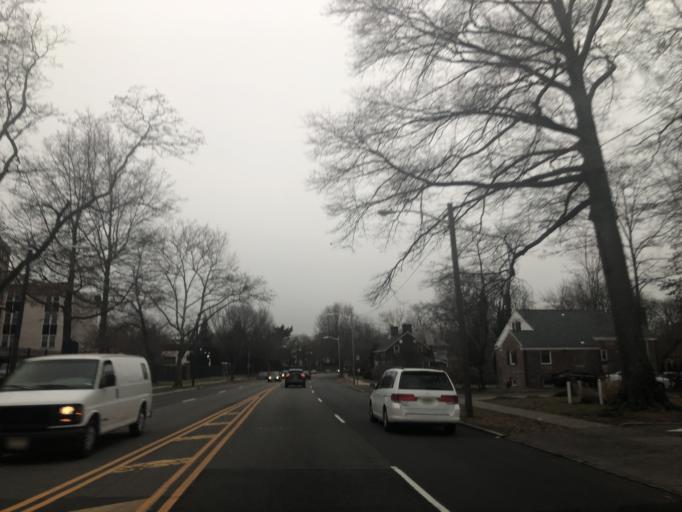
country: US
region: New Jersey
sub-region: Essex County
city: Irvington
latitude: 40.7457
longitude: -74.2435
